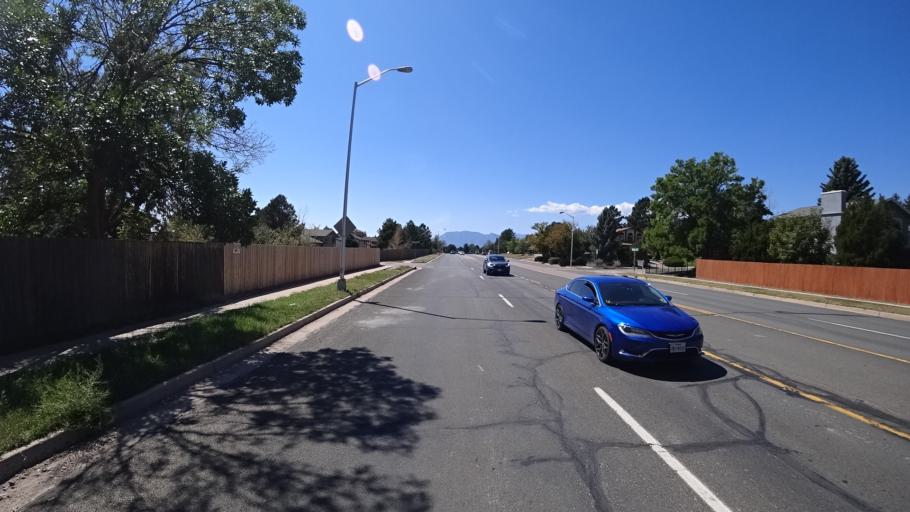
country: US
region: Colorado
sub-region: El Paso County
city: Cimarron Hills
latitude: 38.8707
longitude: -104.7235
